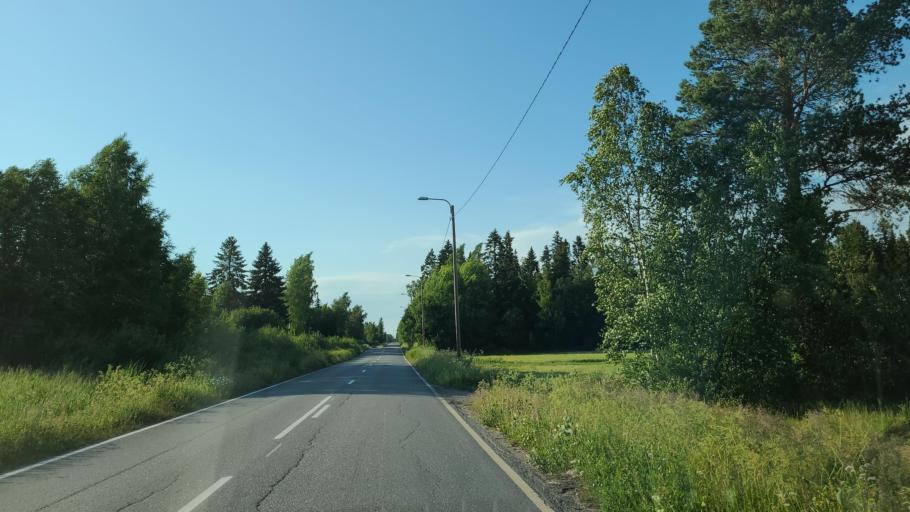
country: FI
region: Ostrobothnia
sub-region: Vaasa
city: Replot
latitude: 63.3255
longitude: 21.3426
